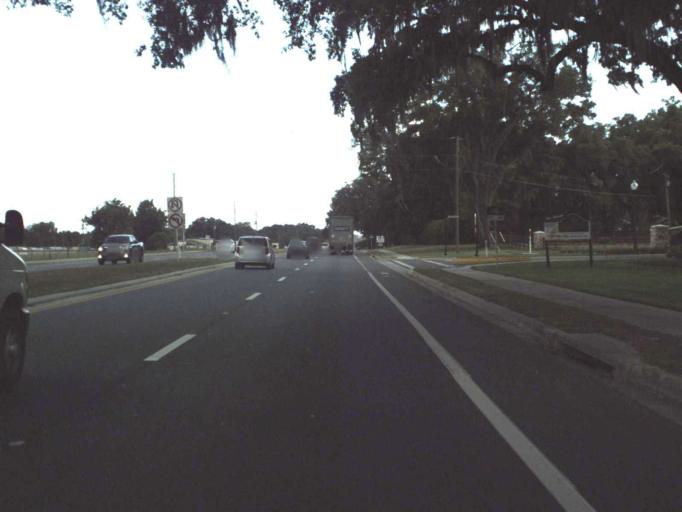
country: US
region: Florida
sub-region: Sumter County
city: Wildwood
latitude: 28.9228
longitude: -82.0373
